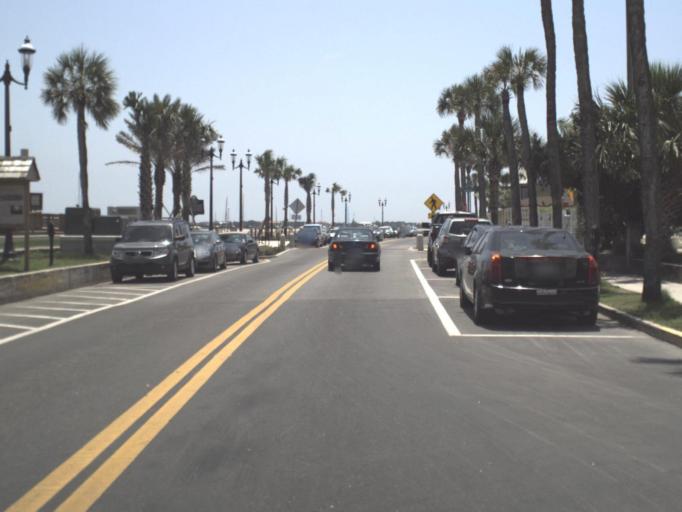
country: US
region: Florida
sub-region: Saint Johns County
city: Saint Augustine
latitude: 29.8911
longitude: -81.3103
